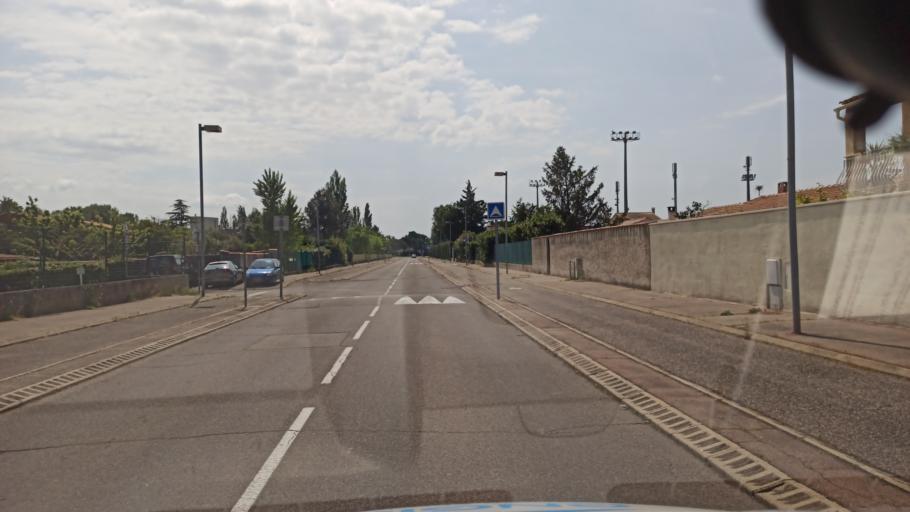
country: FR
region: Provence-Alpes-Cote d'Azur
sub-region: Departement du Vaucluse
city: Le Pontet
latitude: 43.9650
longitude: 4.8748
